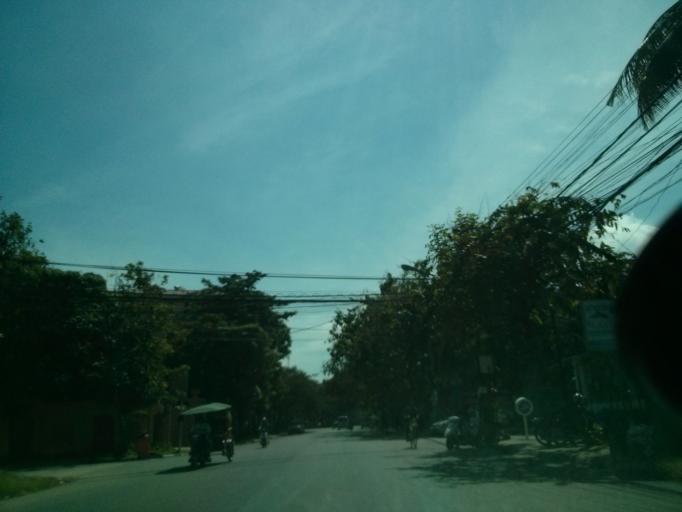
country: KH
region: Phnom Penh
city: Phnom Penh
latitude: 11.5798
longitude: 104.8937
